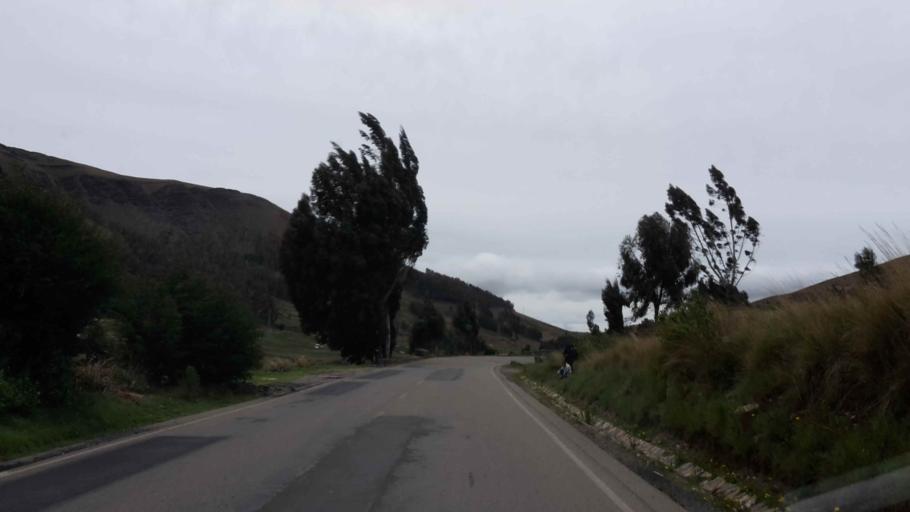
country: BO
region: Cochabamba
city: Arani
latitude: -17.4809
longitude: -65.5730
